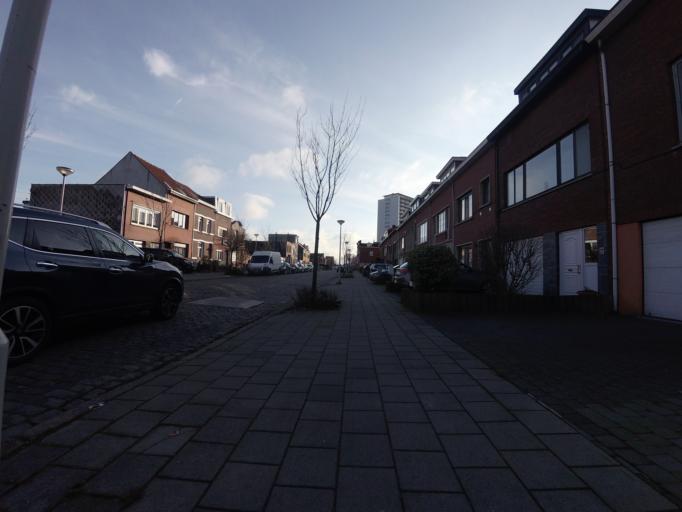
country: BE
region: Flanders
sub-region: Provincie Antwerpen
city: Hoboken
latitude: 51.1793
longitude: 4.3811
